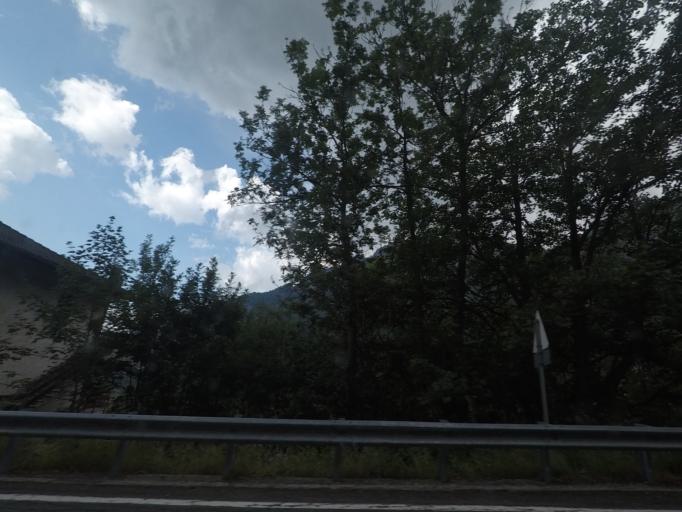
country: IT
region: Aosta Valley
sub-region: Valle d'Aosta
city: Paquier
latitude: 45.8943
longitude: 7.6241
